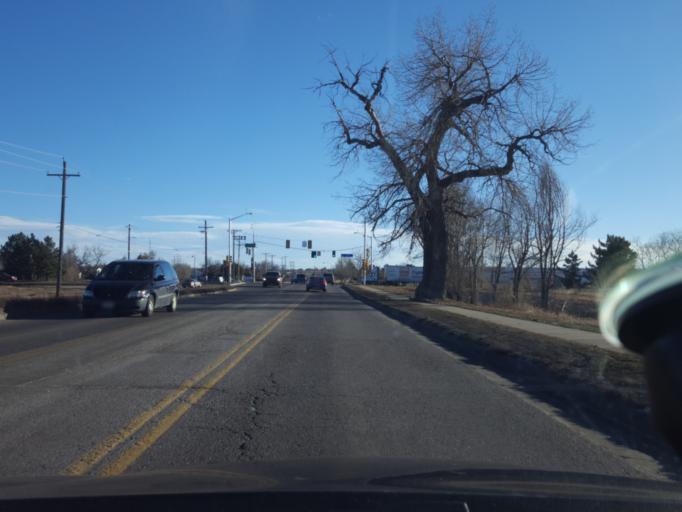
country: US
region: Colorado
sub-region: Adams County
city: Aurora
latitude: 39.7468
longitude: -104.7725
